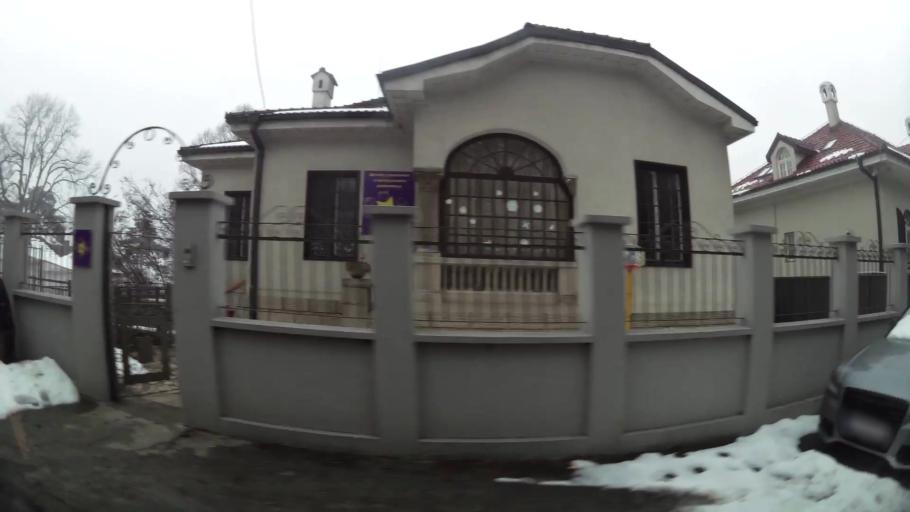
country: RS
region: Central Serbia
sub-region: Belgrade
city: Cukarica
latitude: 44.7858
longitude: 20.4369
